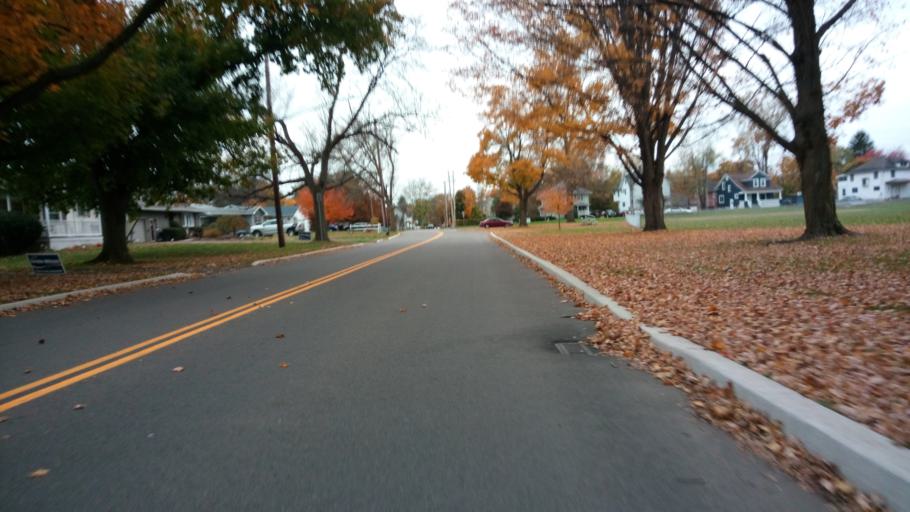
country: US
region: New York
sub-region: Chemung County
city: Elmira
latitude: 42.0853
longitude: -76.7915
